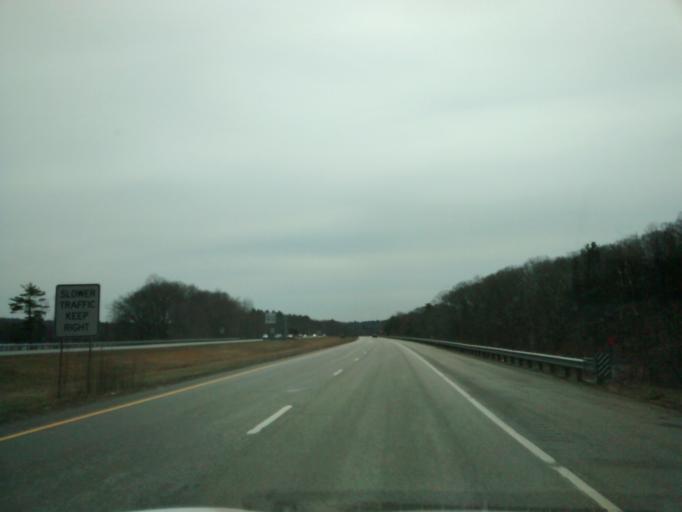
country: US
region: Massachusetts
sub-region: Worcester County
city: Auburn
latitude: 42.1799
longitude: -71.8464
